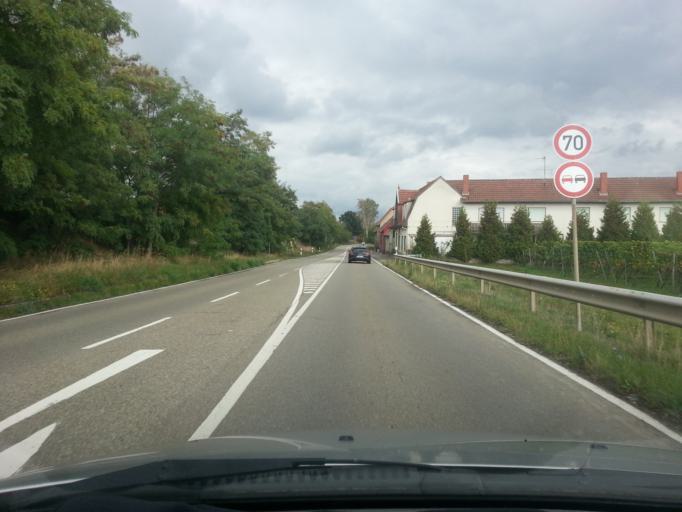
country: DE
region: Rheinland-Pfalz
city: Birkenheide
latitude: 49.4780
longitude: 8.2530
